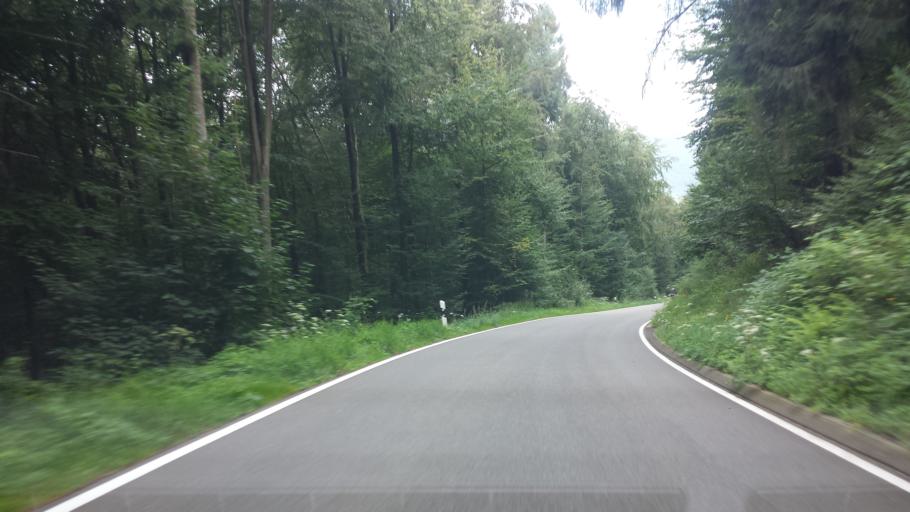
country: DE
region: Rheinland-Pfalz
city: Ramberg
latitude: 49.2688
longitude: 8.0318
